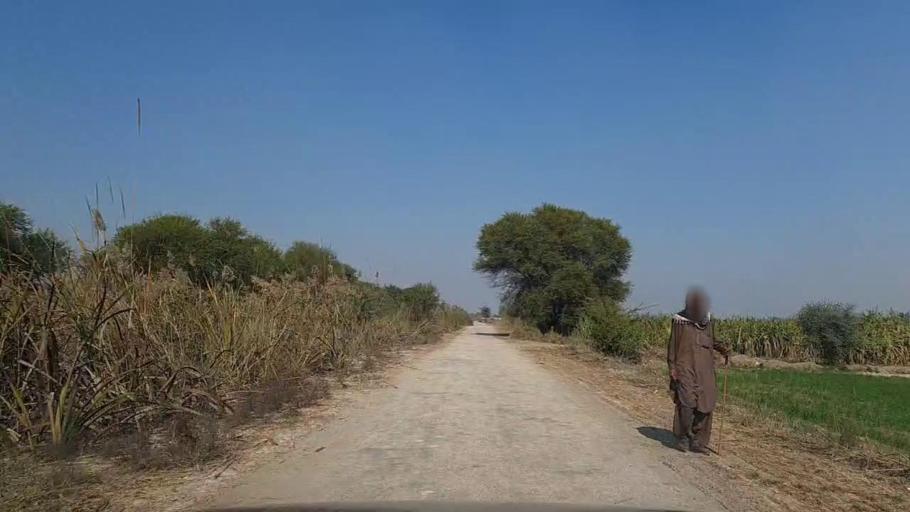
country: PK
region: Sindh
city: Daur
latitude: 26.5022
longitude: 68.3463
